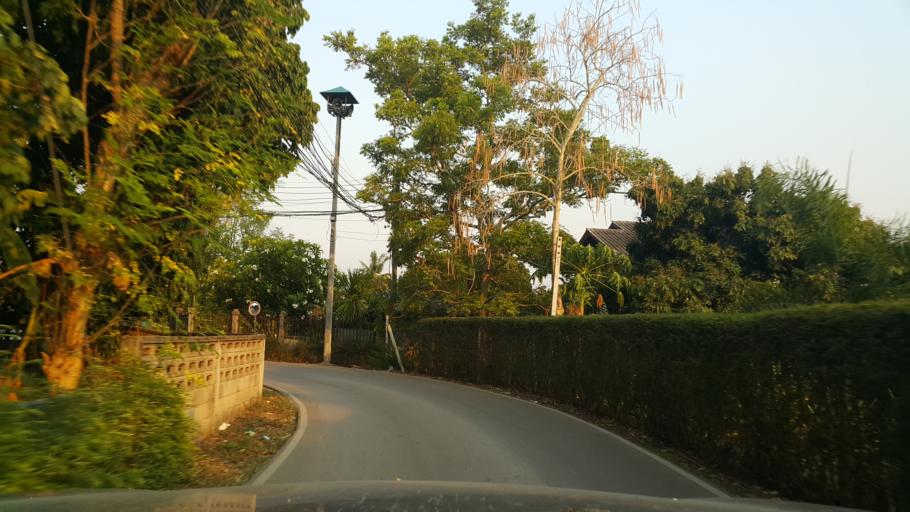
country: TH
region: Chiang Mai
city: Saraphi
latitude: 18.7184
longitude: 99.0246
